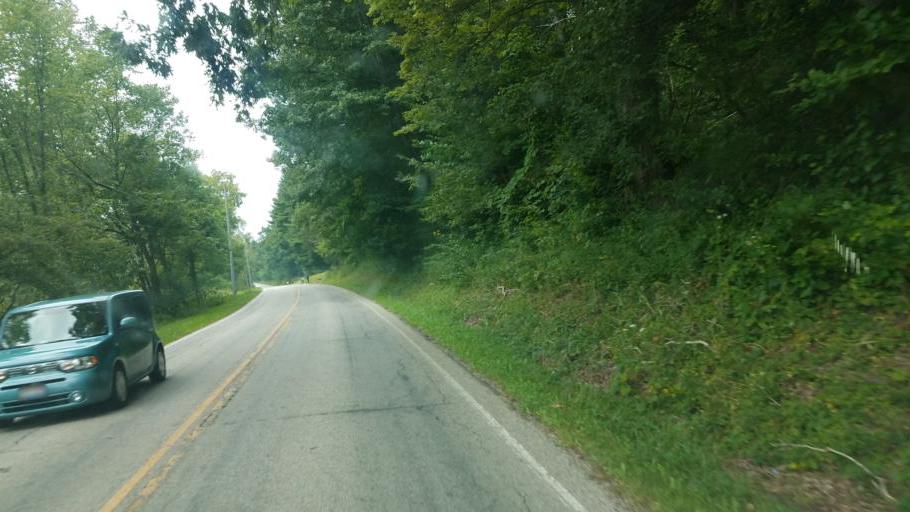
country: US
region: Ohio
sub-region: Sandusky County
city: Bellville
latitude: 40.6549
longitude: -82.4806
